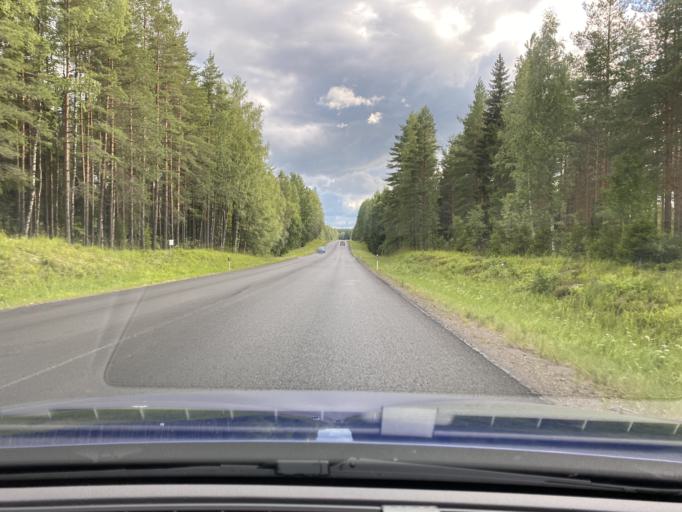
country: FI
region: Haeme
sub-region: Haemeenlinna
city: Renko
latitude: 60.9320
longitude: 24.3612
